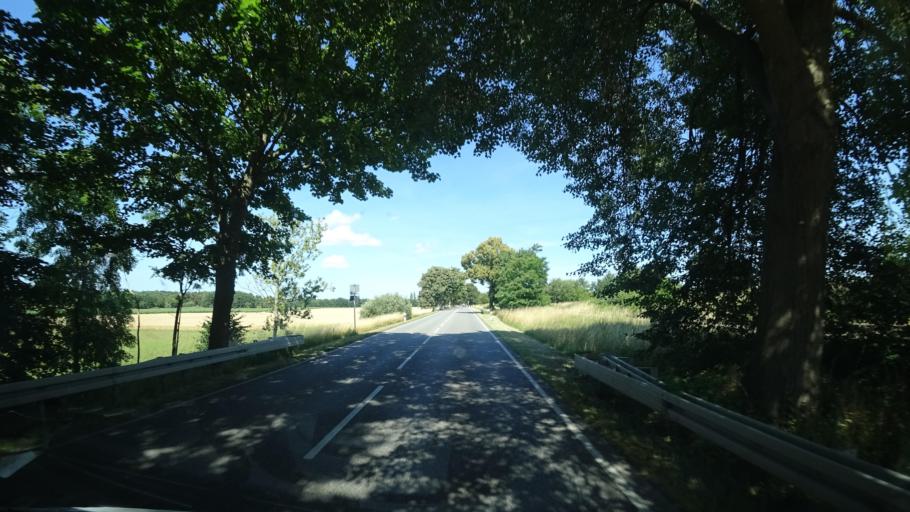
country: DE
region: Mecklenburg-Vorpommern
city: Neubukow
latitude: 54.0392
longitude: 11.6936
